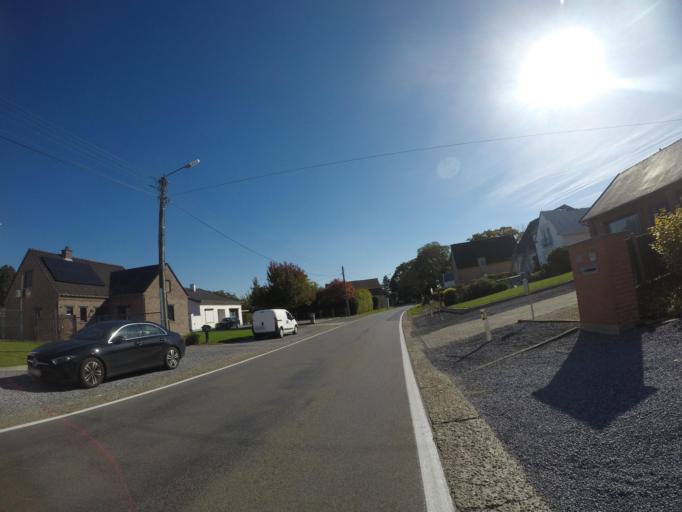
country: BE
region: Flanders
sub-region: Provincie Limburg
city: Alken
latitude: 50.8821
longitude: 5.2746
